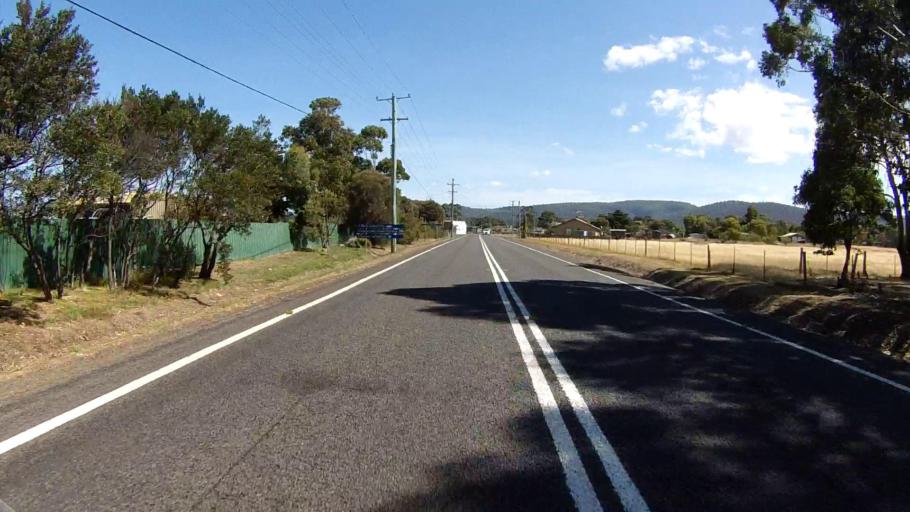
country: AU
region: Tasmania
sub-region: Sorell
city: Sorell
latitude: -42.5009
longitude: 147.9172
